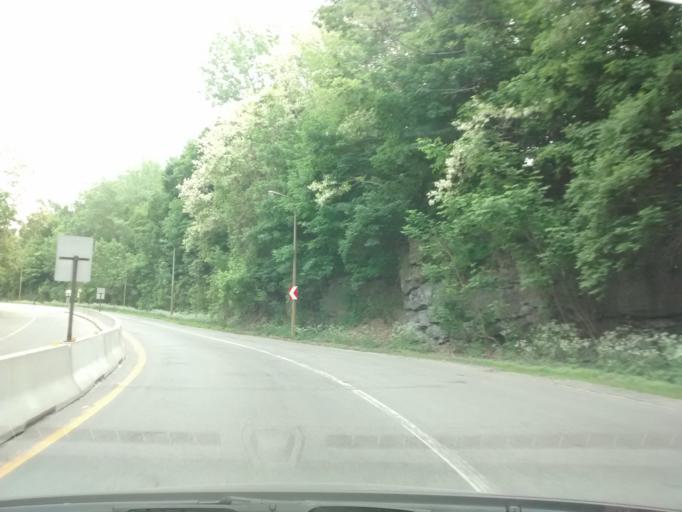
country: CA
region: Quebec
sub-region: Montreal
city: Montreal
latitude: 45.5118
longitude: -73.5968
